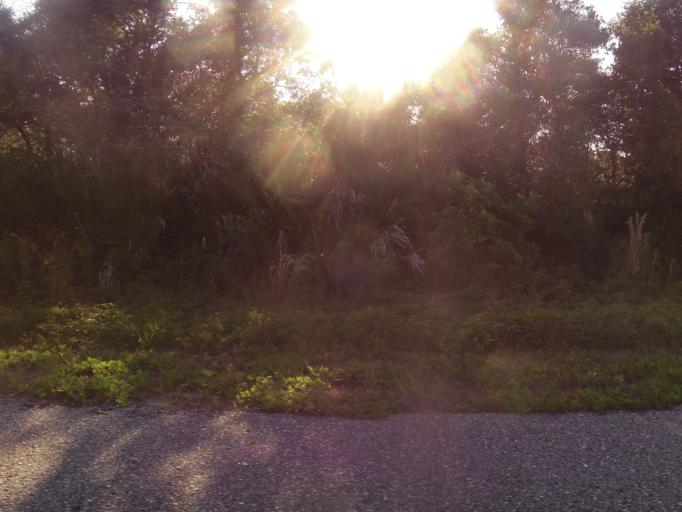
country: US
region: Florida
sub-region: Duval County
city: Atlantic Beach
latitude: 30.4794
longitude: -81.4368
